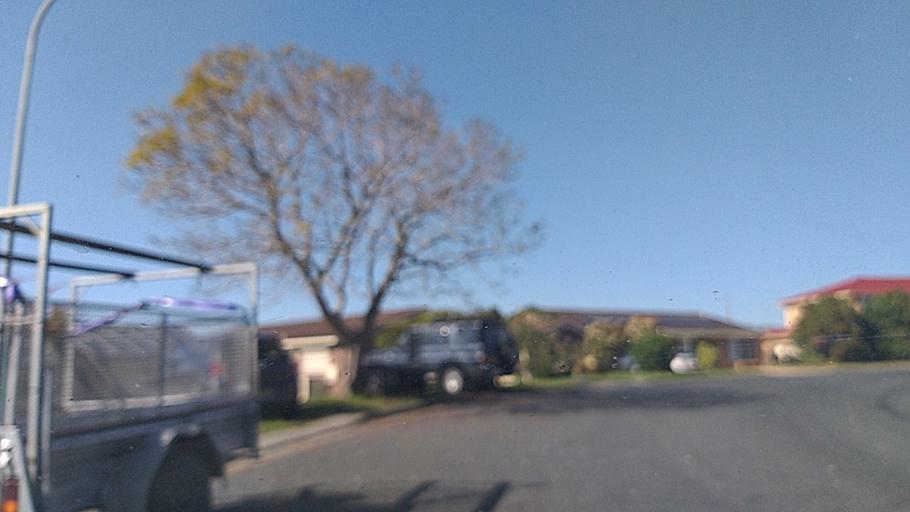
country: AU
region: New South Wales
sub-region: Wollongong
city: Dapto
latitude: -34.4928
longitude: 150.7800
